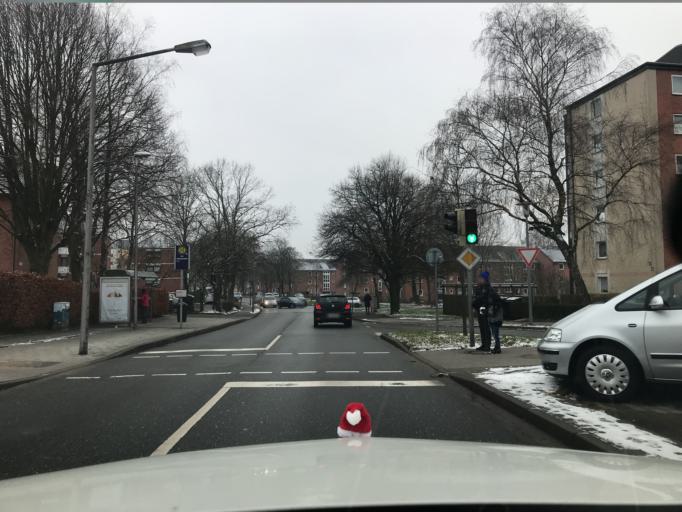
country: DE
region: Schleswig-Holstein
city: Flensburg
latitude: 54.7823
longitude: 9.4170
